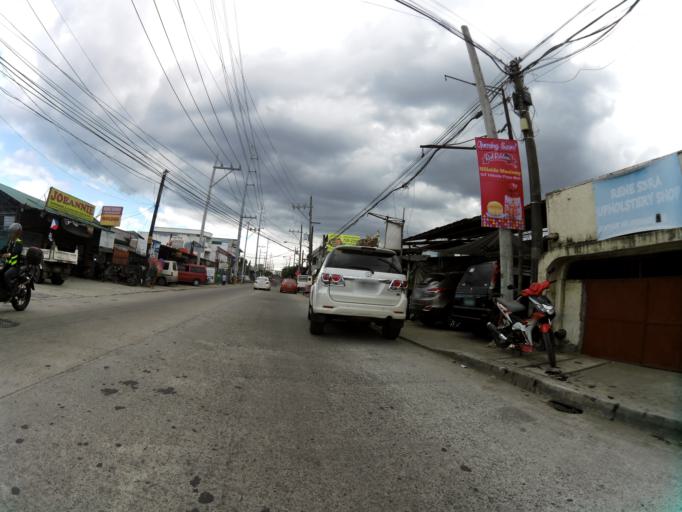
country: PH
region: Calabarzon
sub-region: Province of Rizal
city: Antipolo
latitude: 14.6350
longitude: 121.1215
